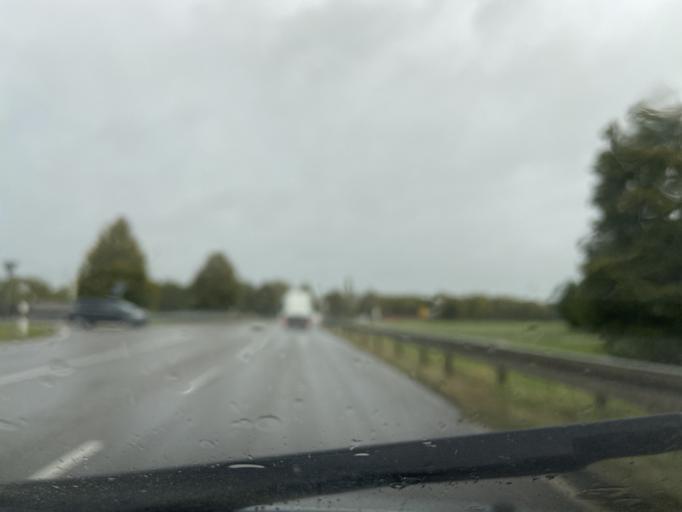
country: DE
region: Baden-Wuerttemberg
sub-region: Tuebingen Region
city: Ennetach
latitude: 48.0485
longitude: 9.3214
